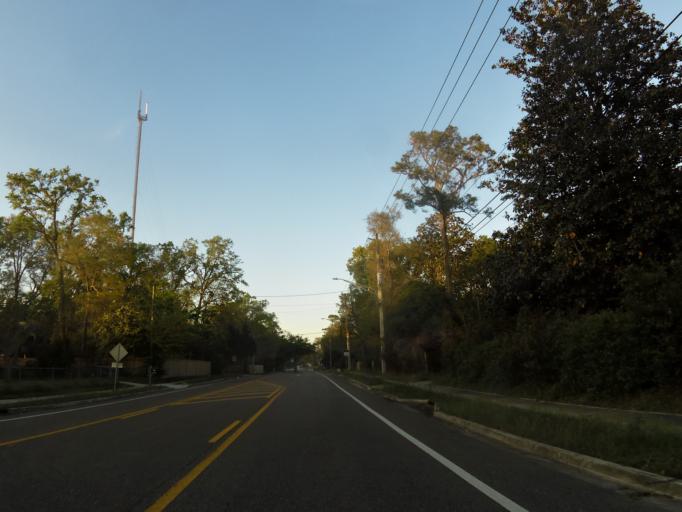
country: US
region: Florida
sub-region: Duval County
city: Jacksonville
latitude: 30.2764
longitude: -81.5707
